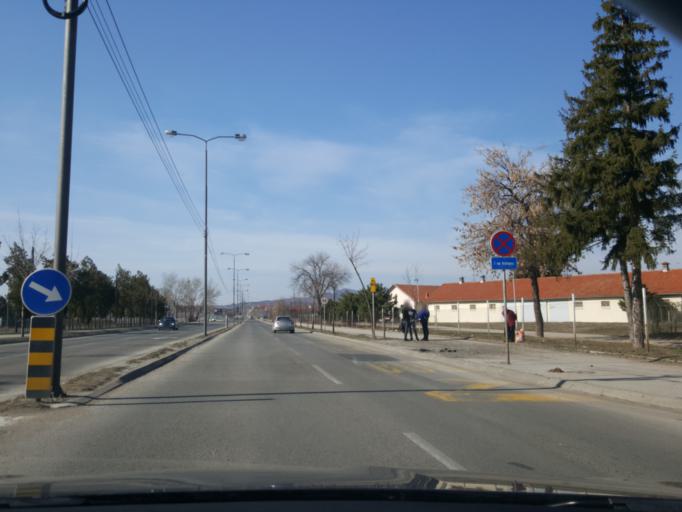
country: RS
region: Central Serbia
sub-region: Nisavski Okrug
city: Nis
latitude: 43.3350
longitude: 21.8919
